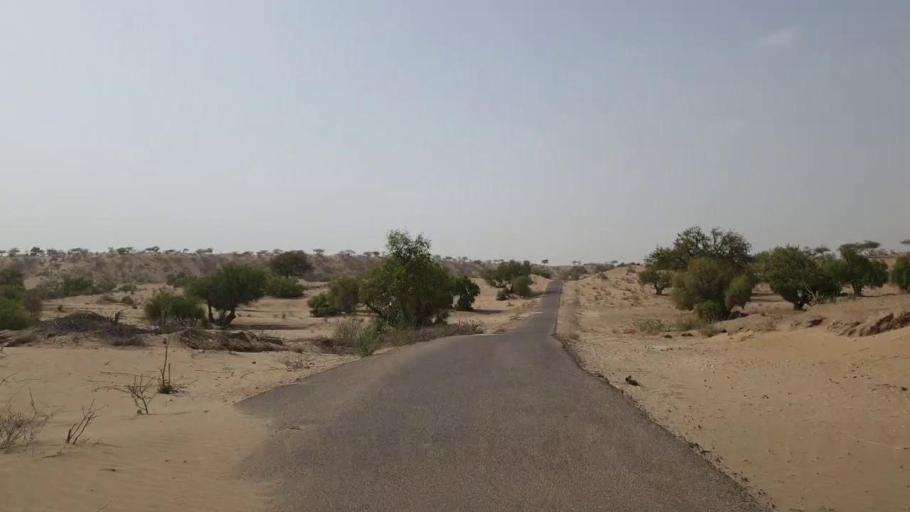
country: PK
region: Sindh
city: Mithi
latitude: 24.5810
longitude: 69.9234
